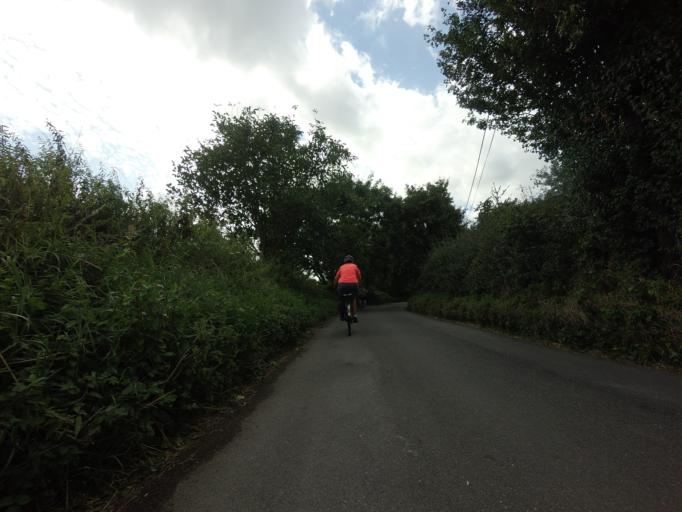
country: GB
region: England
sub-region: Kent
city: Shoreham
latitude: 51.3131
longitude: 0.1695
